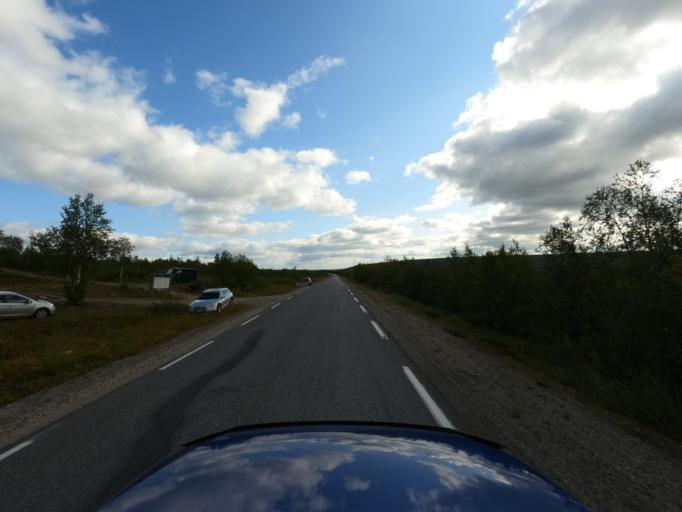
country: NO
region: Finnmark Fylke
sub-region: Porsanger
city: Lakselv
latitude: 69.3739
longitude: 24.4050
